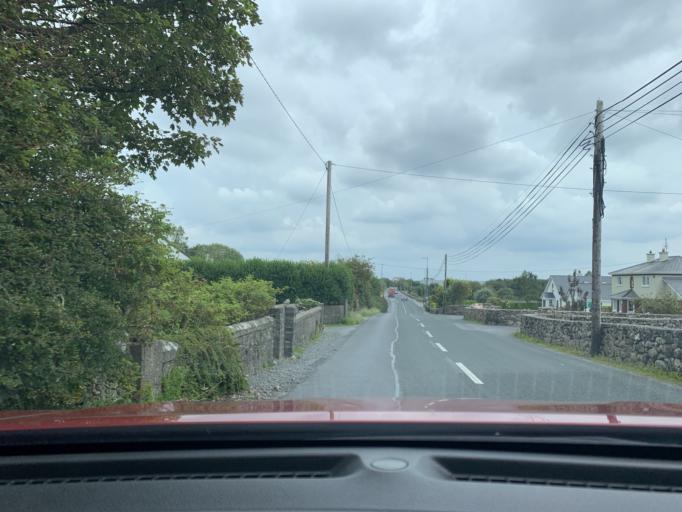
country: IE
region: Connaught
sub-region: County Galway
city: Gaillimh
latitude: 53.2777
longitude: -9.0997
